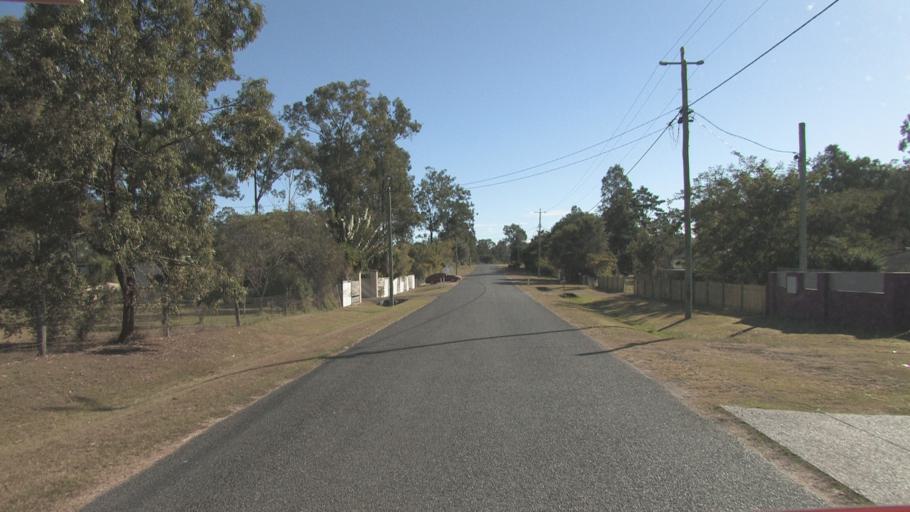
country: AU
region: Queensland
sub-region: Logan
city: North Maclean
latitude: -27.8073
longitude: 152.9788
